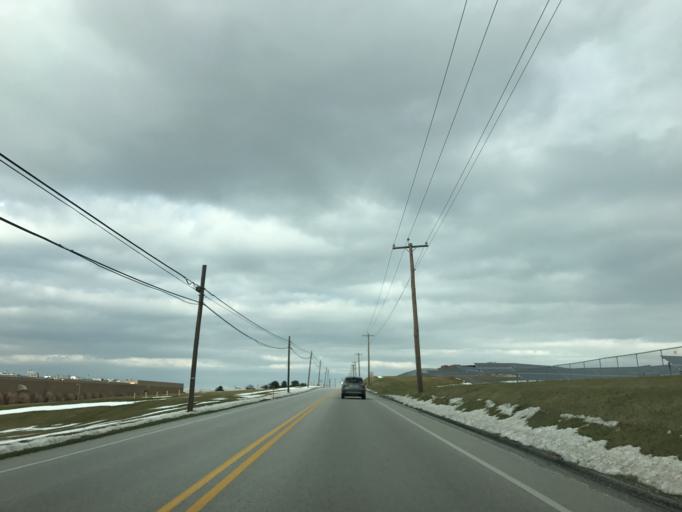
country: US
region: Pennsylvania
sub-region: York County
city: Parkville
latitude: 39.8036
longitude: -76.9515
